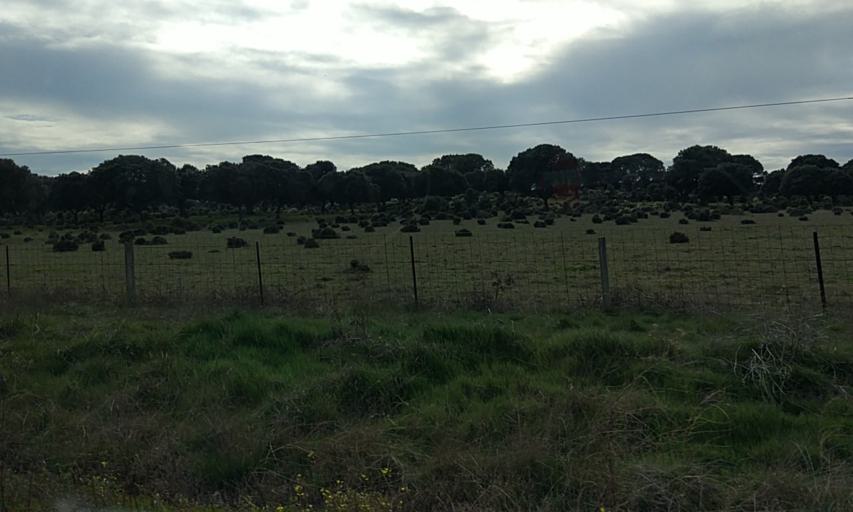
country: ES
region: Castille and Leon
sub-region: Provincia de Salamanca
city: Herguijuela de Ciudad Rodrigo
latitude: 40.4554
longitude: -6.5904
